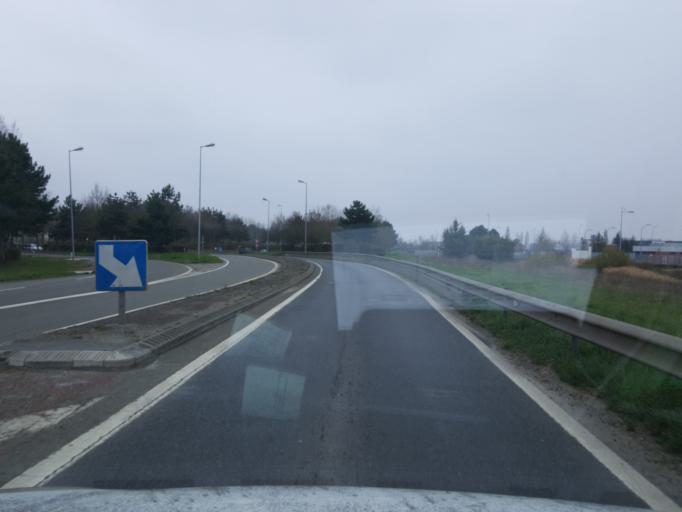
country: FR
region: Centre
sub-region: Departement d'Eure-et-Loir
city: Vernouillet
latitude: 48.7120
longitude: 1.3688
